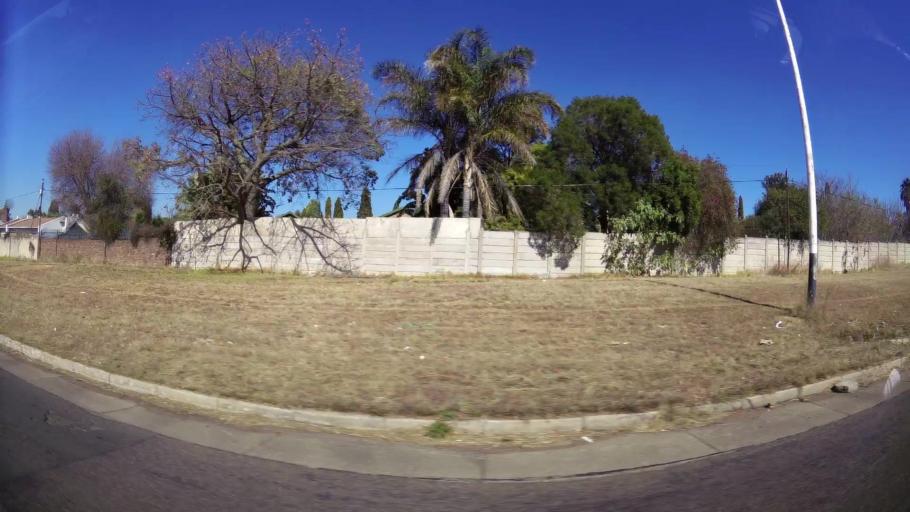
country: ZA
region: Mpumalanga
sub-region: Nkangala District Municipality
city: Witbank
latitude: -25.8632
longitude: 29.2407
